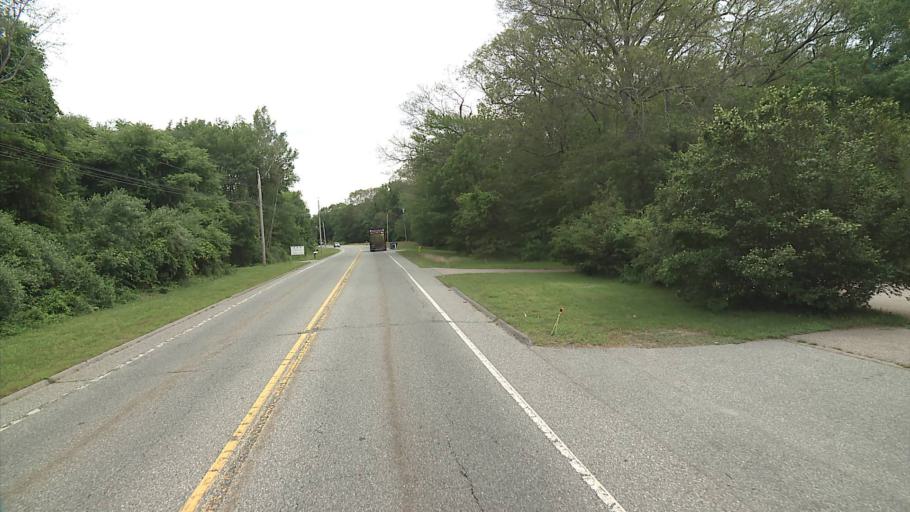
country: US
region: Connecticut
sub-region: New London County
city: Conning Towers-Nautilus Park
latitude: 41.3915
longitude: -72.0273
